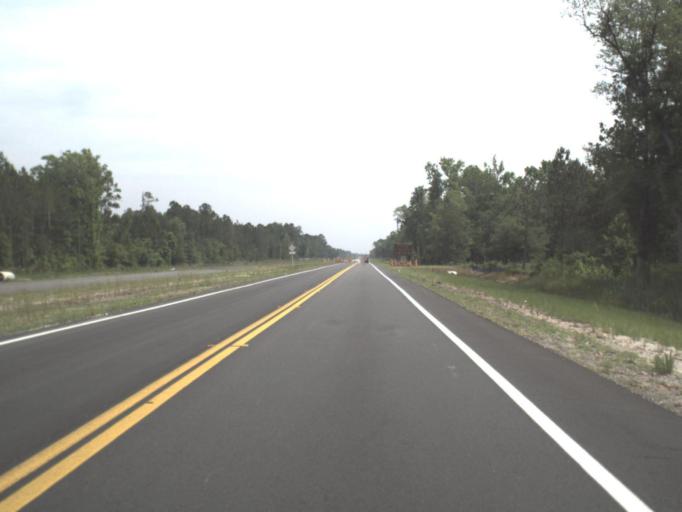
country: US
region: Florida
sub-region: Nassau County
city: Nassau Village-Ratliff
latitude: 30.4357
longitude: -81.9212
